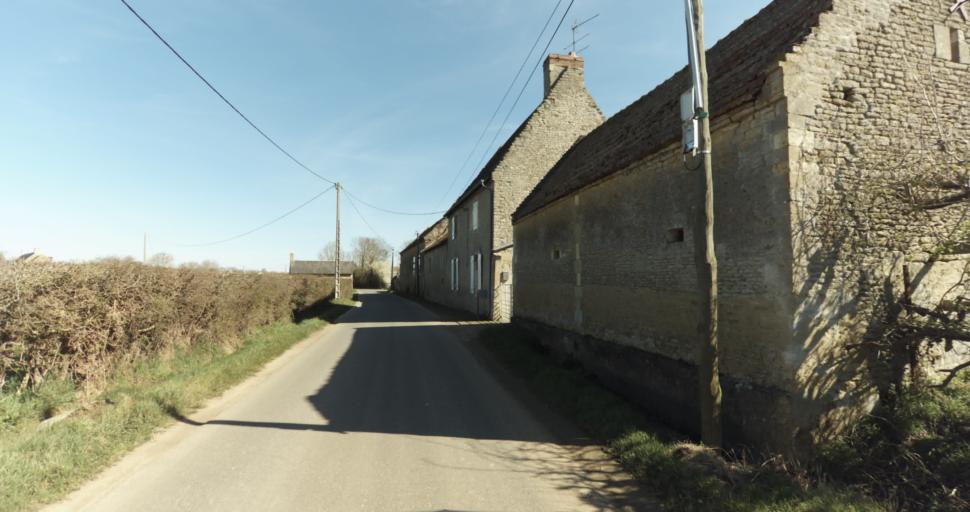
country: FR
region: Lower Normandy
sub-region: Departement du Calvados
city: Saint-Pierre-sur-Dives
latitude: 49.0501
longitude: -0.0341
